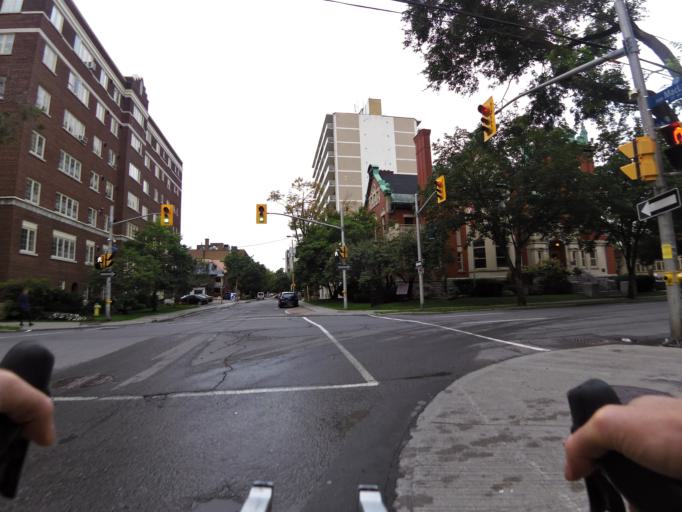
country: CA
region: Ontario
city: Ottawa
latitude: 45.4164
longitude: -75.6917
